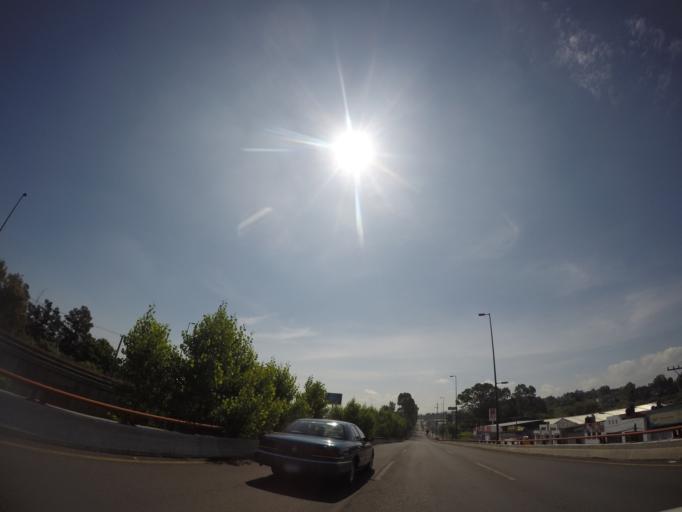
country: MX
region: Michoacan
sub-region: Tarimbaro
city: Real Hacienda (Metropolis)
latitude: 19.7253
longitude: -101.2043
